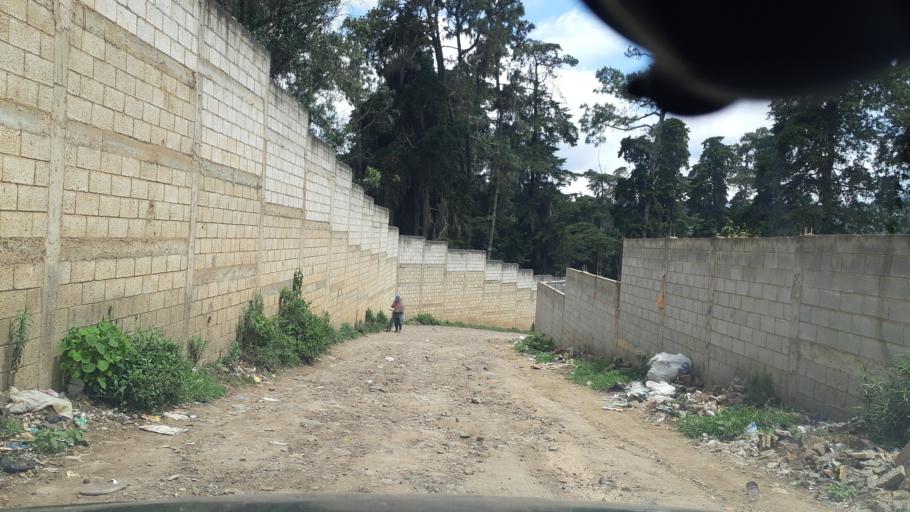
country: GT
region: Chimaltenango
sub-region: Municipio de Chimaltenango
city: Chimaltenango
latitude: 14.6621
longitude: -90.8426
